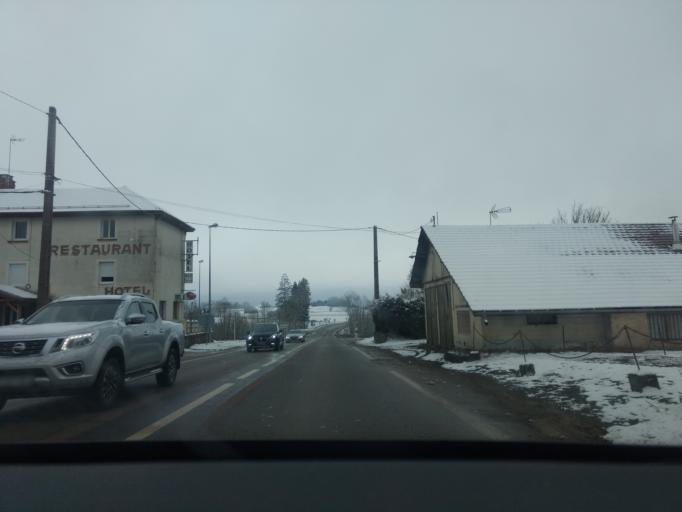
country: FR
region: Franche-Comte
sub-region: Departement du Jura
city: Champagnole
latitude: 46.7801
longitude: 5.8951
